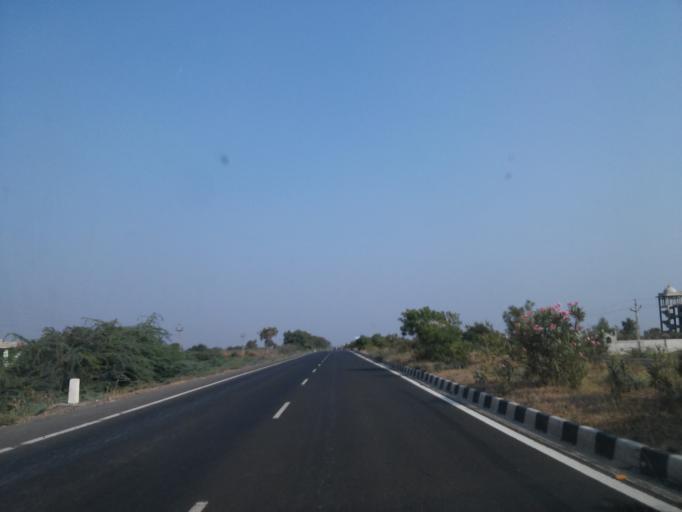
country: IN
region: Gujarat
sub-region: Surendranagar
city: Halvad
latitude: 23.0052
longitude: 71.1097
